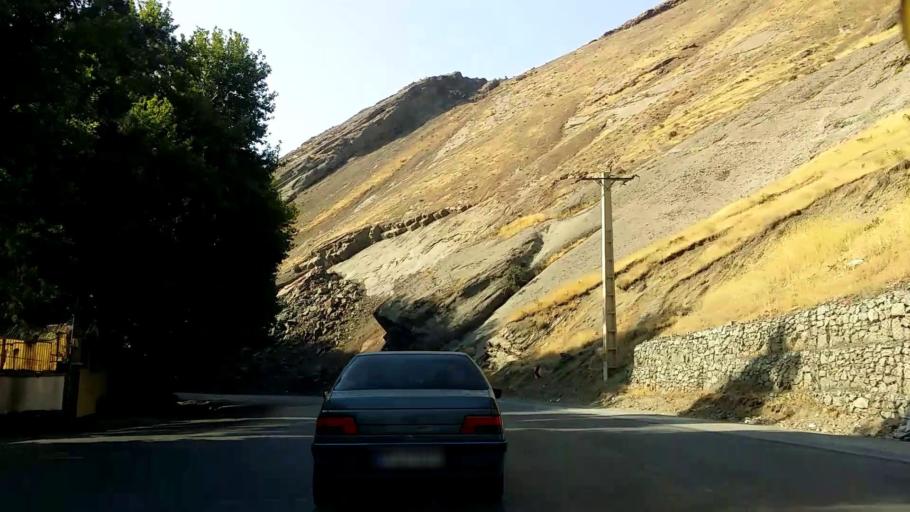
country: IR
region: Alborz
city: Karaj
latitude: 35.8632
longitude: 51.0532
